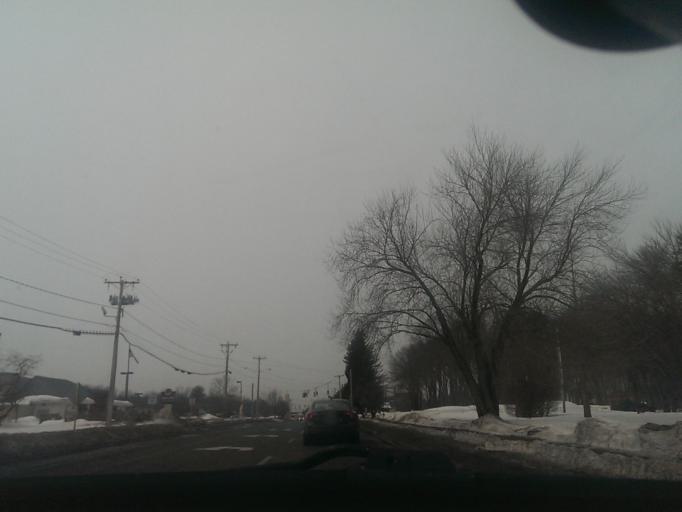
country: US
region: Massachusetts
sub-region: Hampden County
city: East Longmeadow
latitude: 42.0779
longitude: -72.5239
